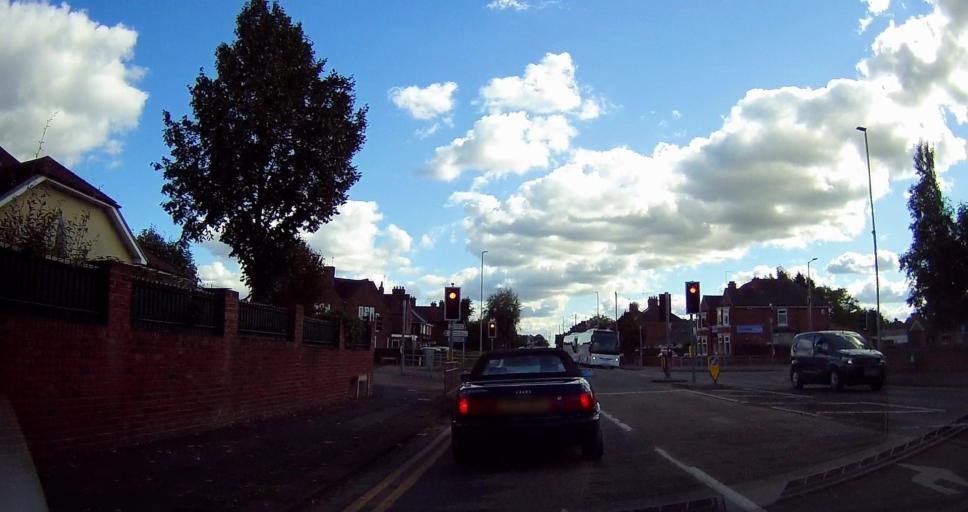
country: GB
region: England
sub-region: Staffordshire
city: Stafford
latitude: 52.8240
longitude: -2.1279
